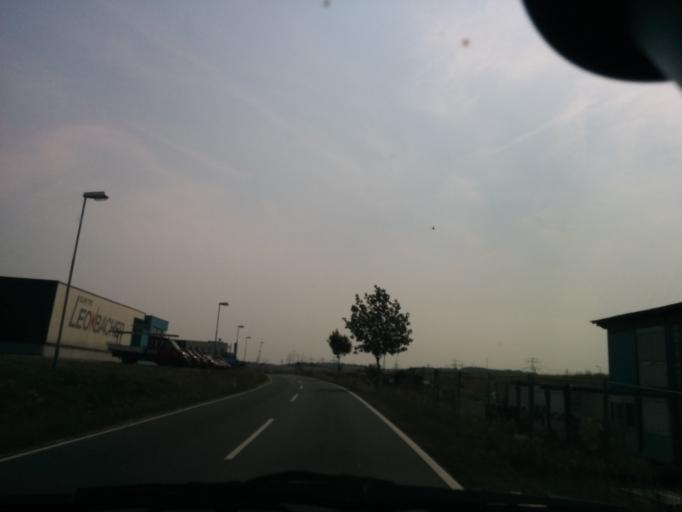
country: AT
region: Lower Austria
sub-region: Politischer Bezirk Korneuburg
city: Harmannsdorf
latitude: 48.3651
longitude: 16.3590
